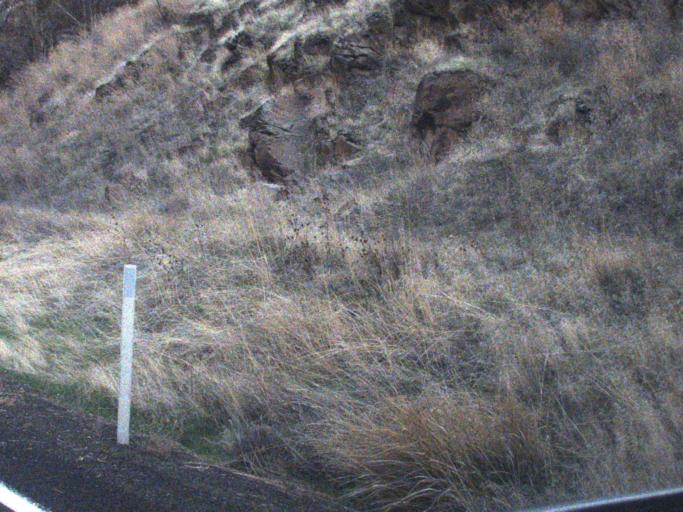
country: US
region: Washington
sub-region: Walla Walla County
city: Waitsburg
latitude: 46.5394
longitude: -118.1547
